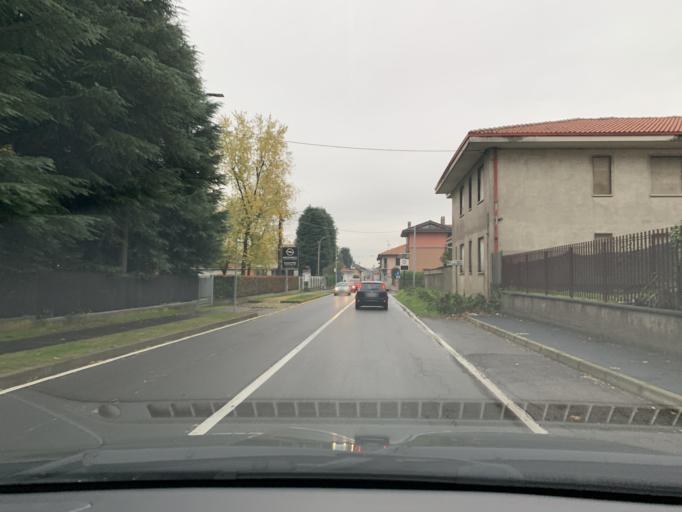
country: IT
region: Lombardy
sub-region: Provincia di Como
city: Rovello Porro
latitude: 45.6405
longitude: 9.0472
